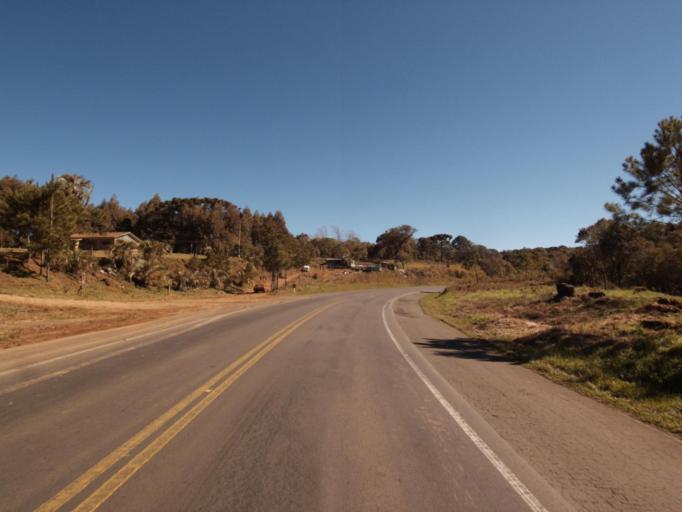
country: BR
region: Santa Catarina
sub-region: Concordia
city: Concordia
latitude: -26.9210
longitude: -51.9519
